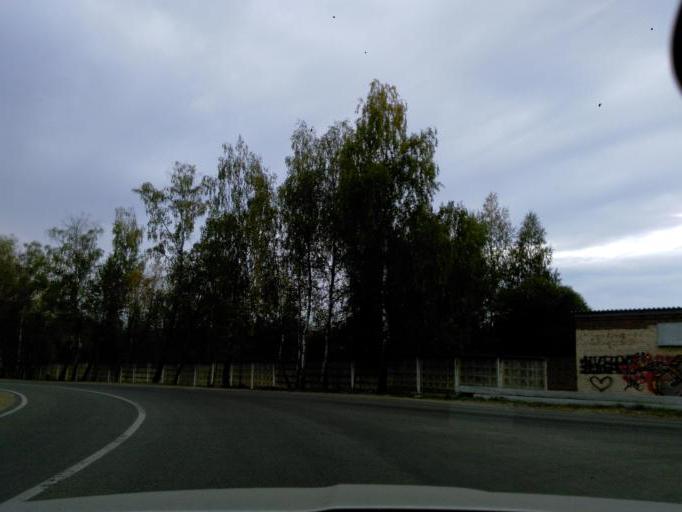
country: RU
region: Moskovskaya
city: Andreyevka
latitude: 55.9807
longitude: 37.1195
